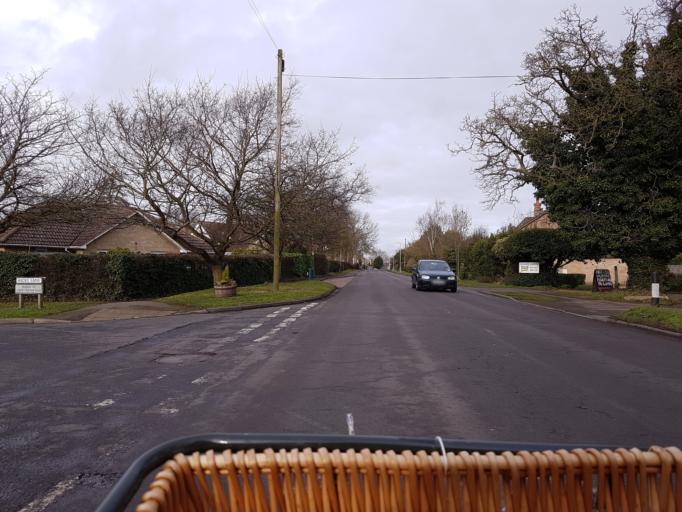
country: GB
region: England
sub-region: Cambridgeshire
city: Girton
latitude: 52.2363
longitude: 0.0855
